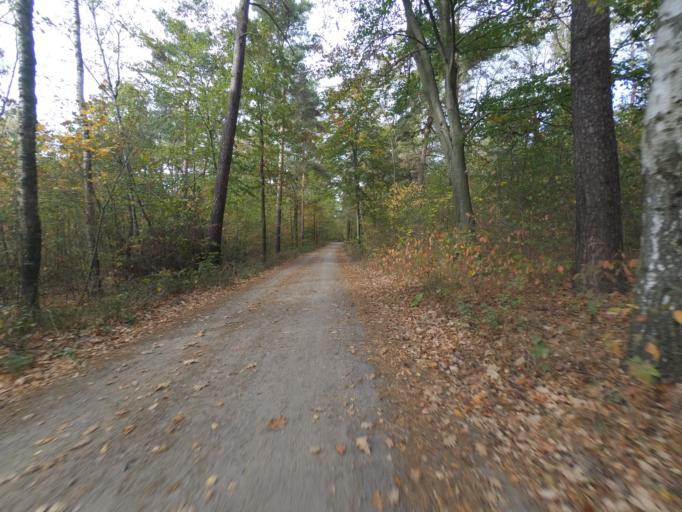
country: DE
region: Saxony
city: Albertstadt
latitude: 51.0854
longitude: 13.7832
